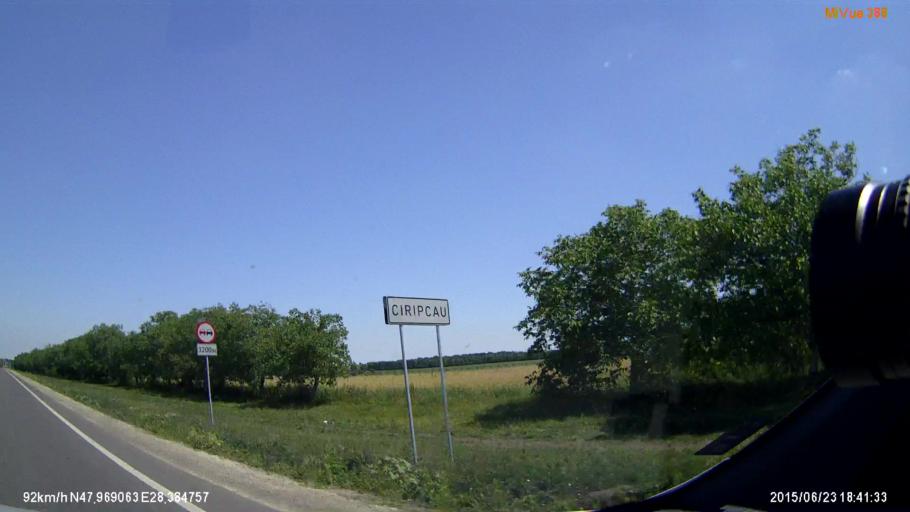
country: MD
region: Floresti
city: Leninskiy
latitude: 47.9684
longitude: 28.3848
